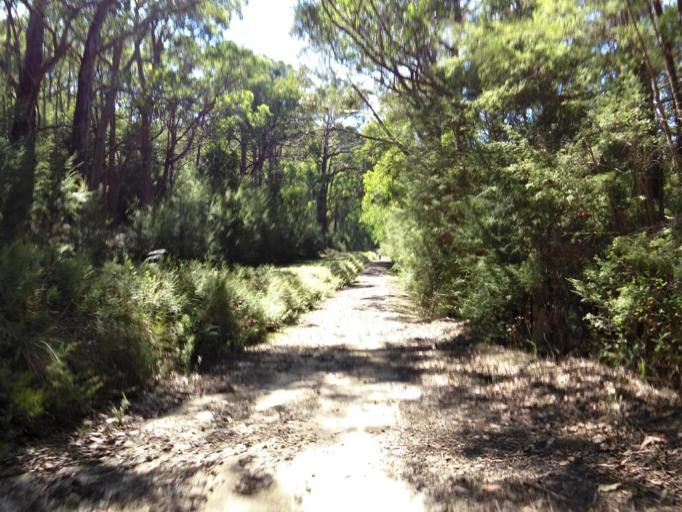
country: AU
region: Victoria
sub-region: Yarra Ranges
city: Launching Place
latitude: -37.7448
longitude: 145.5538
